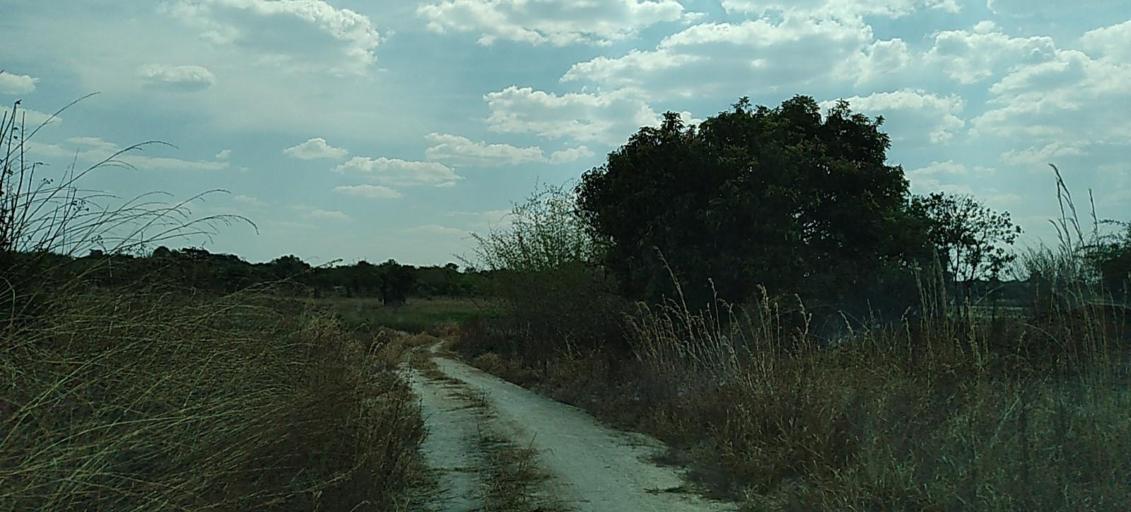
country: ZM
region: Copperbelt
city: Chililabombwe
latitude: -12.3341
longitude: 27.7843
